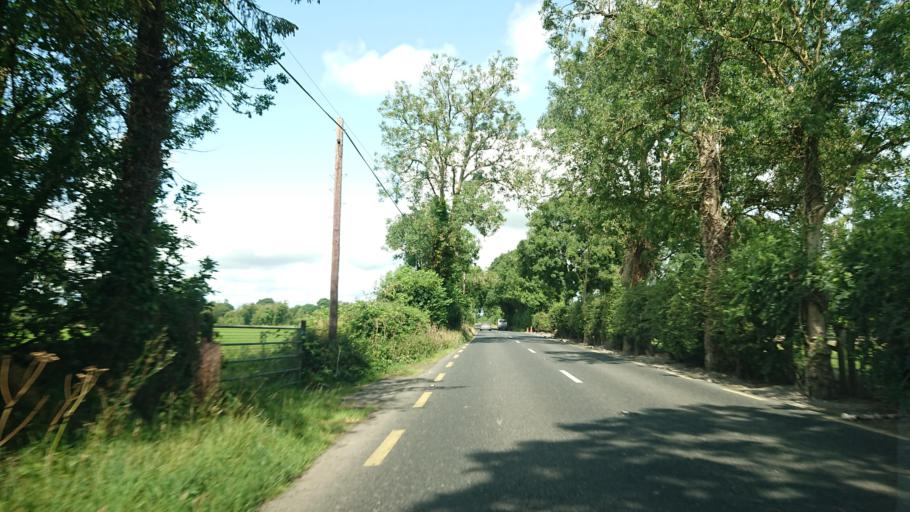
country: IE
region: Leinster
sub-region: Kildare
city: Kilcock
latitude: 53.3582
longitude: -6.6958
